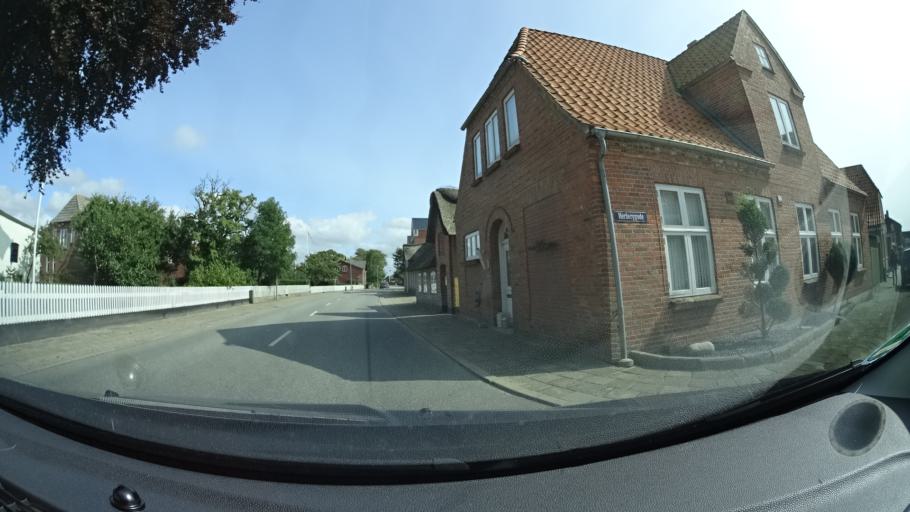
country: DE
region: Schleswig-Holstein
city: Rodenas
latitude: 54.9633
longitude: 8.6989
